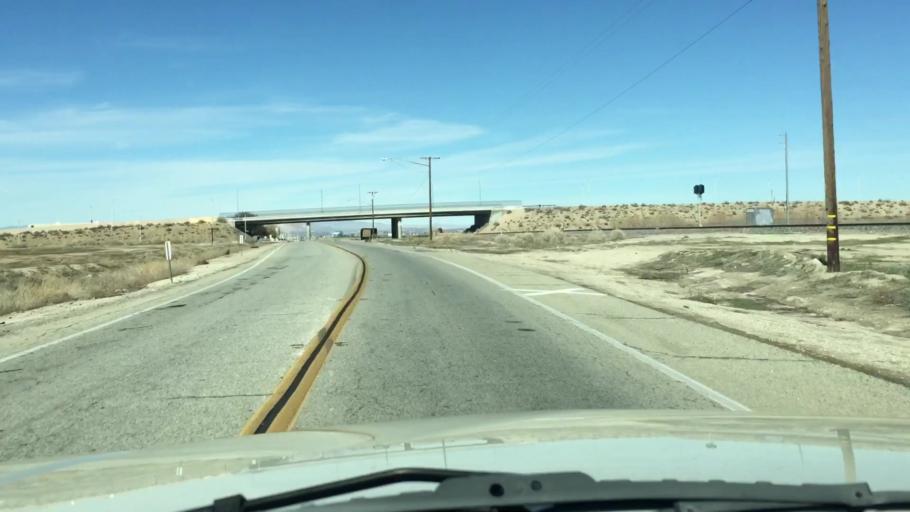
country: US
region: California
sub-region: Los Angeles County
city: Lancaster
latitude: 34.7159
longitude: -118.1395
